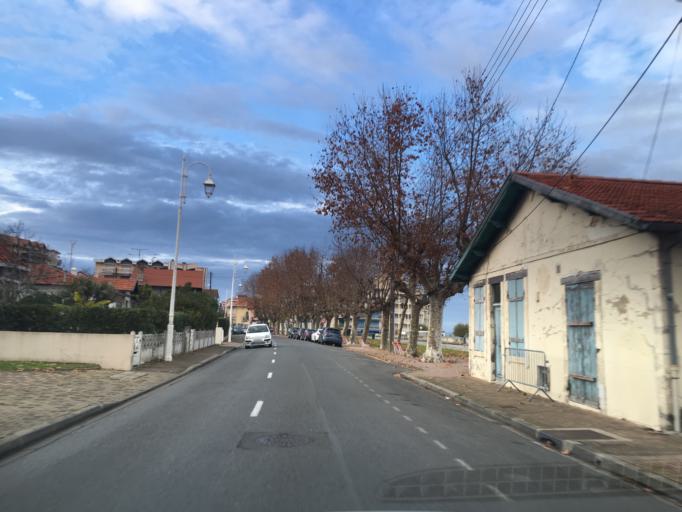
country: FR
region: Aquitaine
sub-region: Departement de la Gironde
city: Arcachon
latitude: 44.6590
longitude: -1.1518
